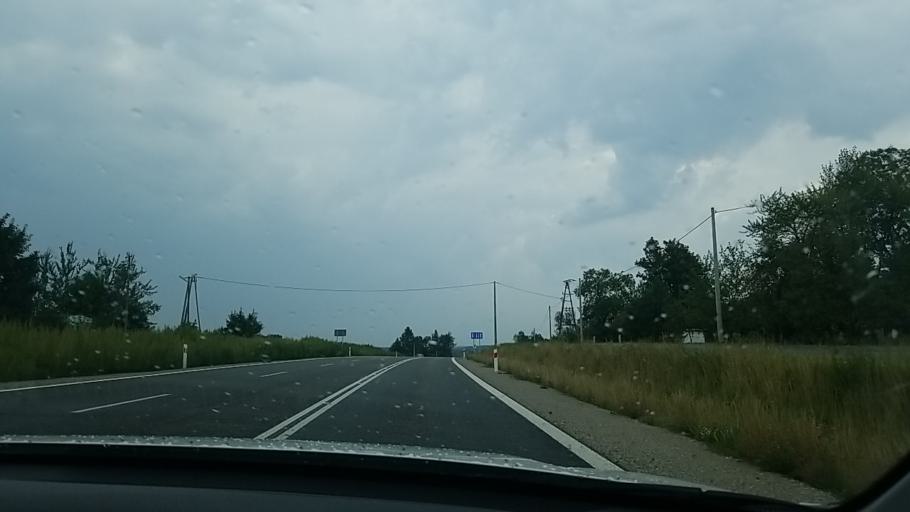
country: PL
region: Lublin Voivodeship
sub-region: Powiat lubelski
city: Krzczonow
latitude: 50.9871
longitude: 22.6777
